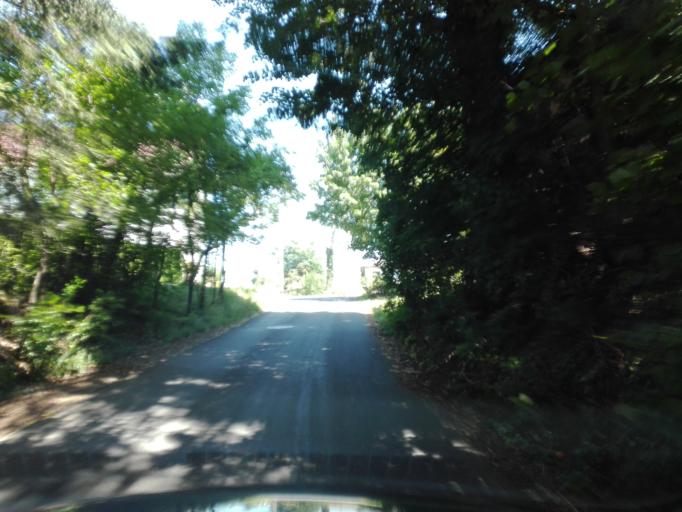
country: AT
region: Upper Austria
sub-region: Politischer Bezirk Urfahr-Umgebung
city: Engerwitzdorf
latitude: 48.2855
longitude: 14.4512
